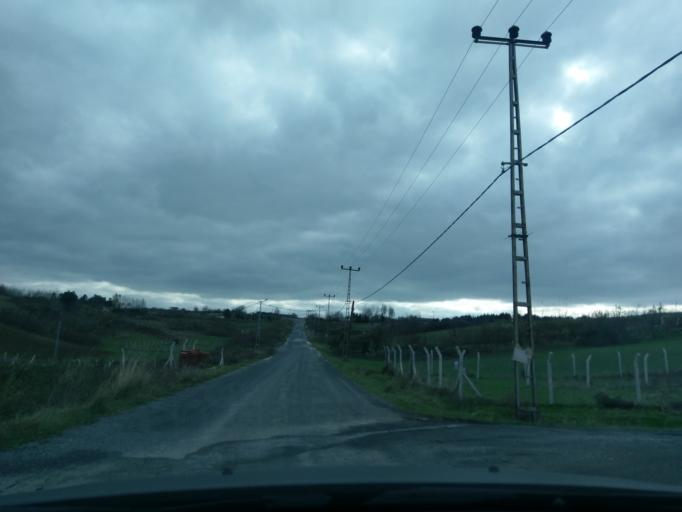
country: TR
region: Istanbul
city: Durusu
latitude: 41.2892
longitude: 28.6877
